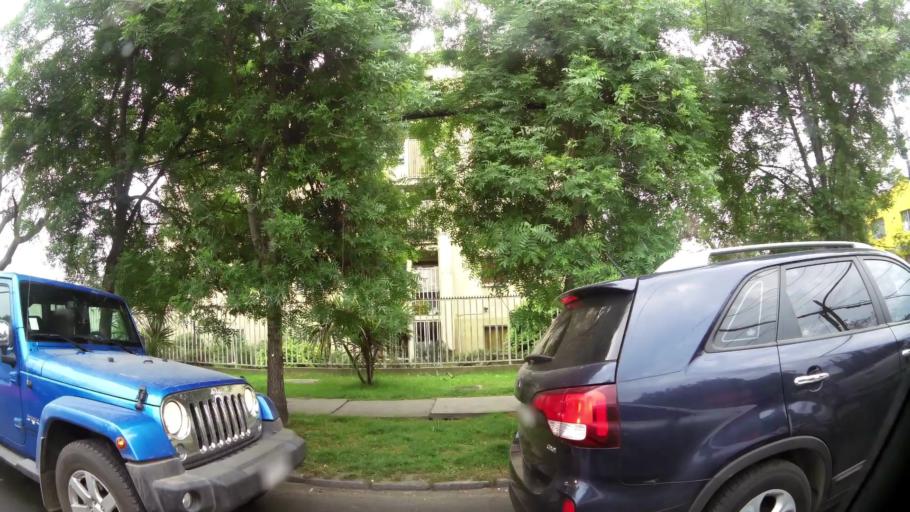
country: CL
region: Santiago Metropolitan
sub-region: Provincia de Santiago
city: Lo Prado
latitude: -33.5013
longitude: -70.7604
